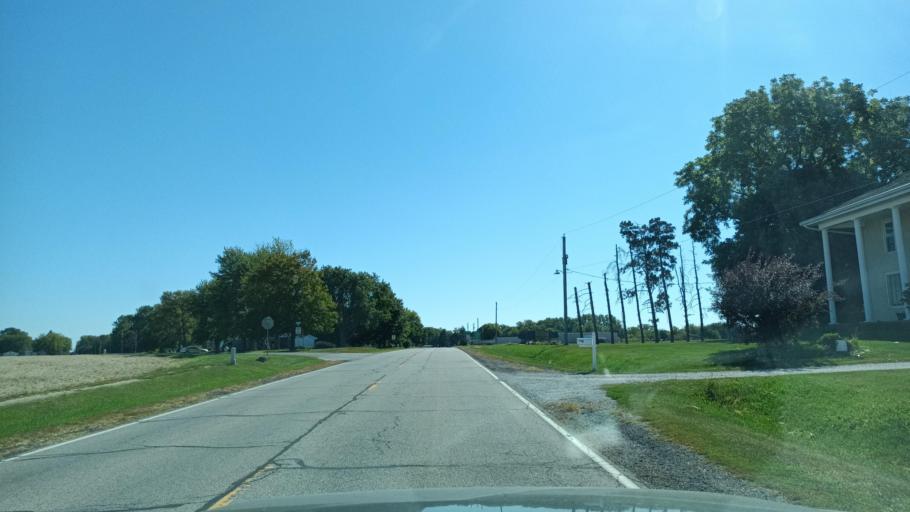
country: US
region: Illinois
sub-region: Peoria County
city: Elmwood
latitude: 40.8415
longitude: -89.8953
